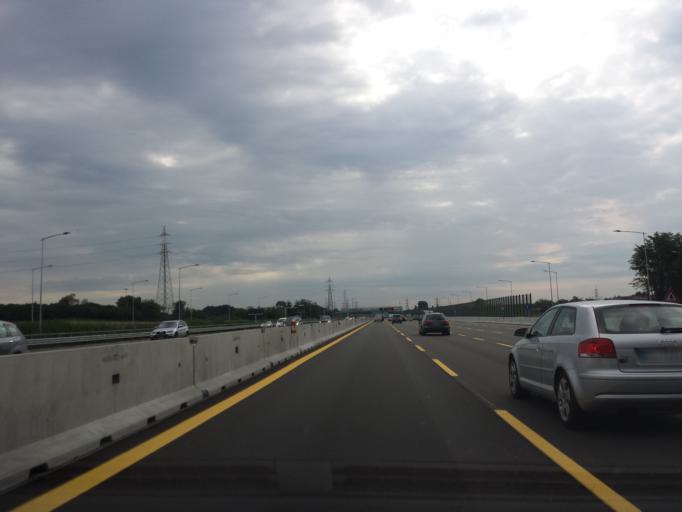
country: IT
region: Lombardy
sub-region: Citta metropolitana di Milano
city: Passirana
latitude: 45.5568
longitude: 9.0440
